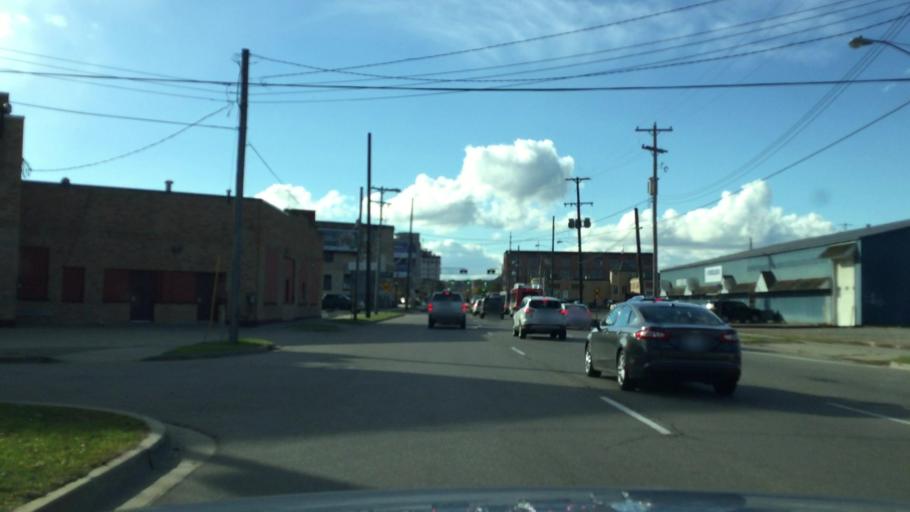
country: US
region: Michigan
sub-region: Kalamazoo County
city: Kalamazoo
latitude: 42.2946
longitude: -85.5764
